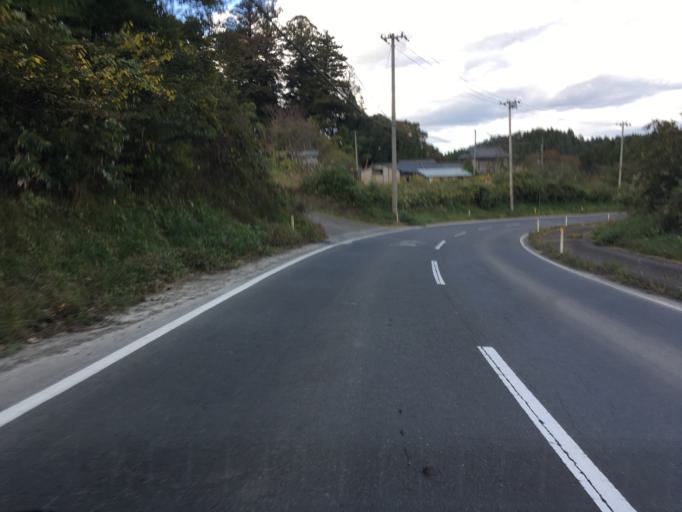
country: JP
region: Miyagi
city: Marumori
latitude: 37.8339
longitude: 140.8331
